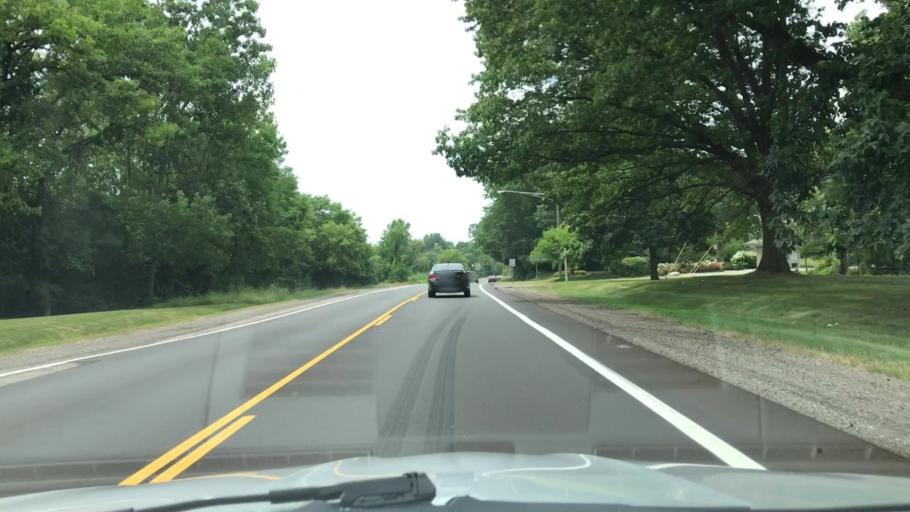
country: US
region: Michigan
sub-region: Oakland County
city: West Bloomfield Township
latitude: 42.5696
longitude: -83.4073
